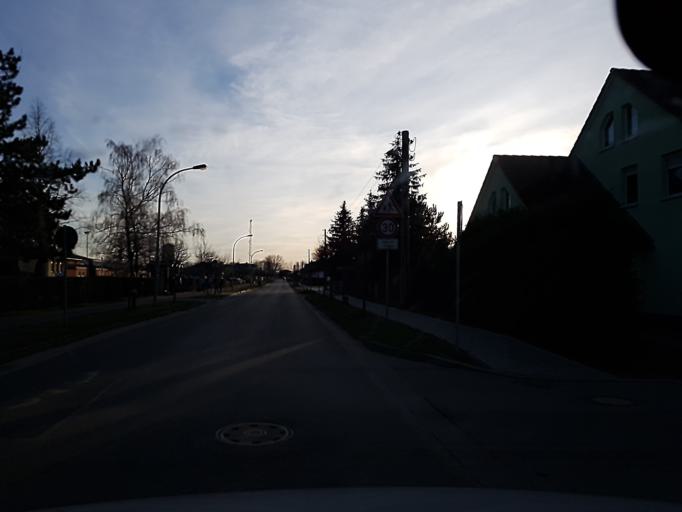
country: DE
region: Brandenburg
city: Finsterwalde
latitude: 51.6413
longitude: 13.7304
